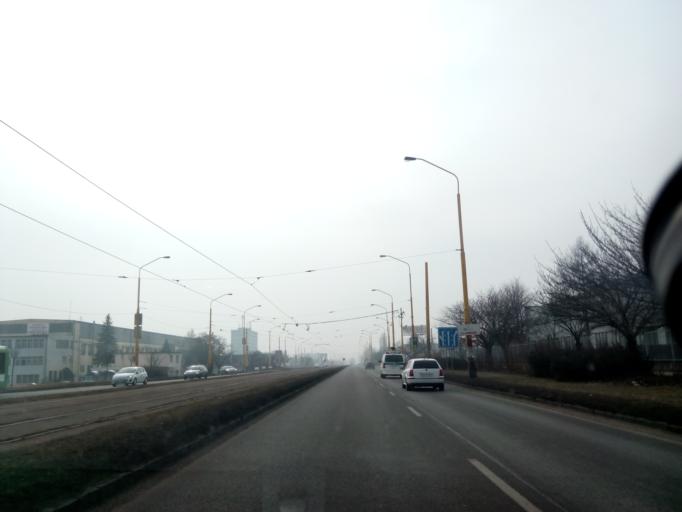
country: SK
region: Kosicky
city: Kosice
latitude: 48.6878
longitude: 21.2663
